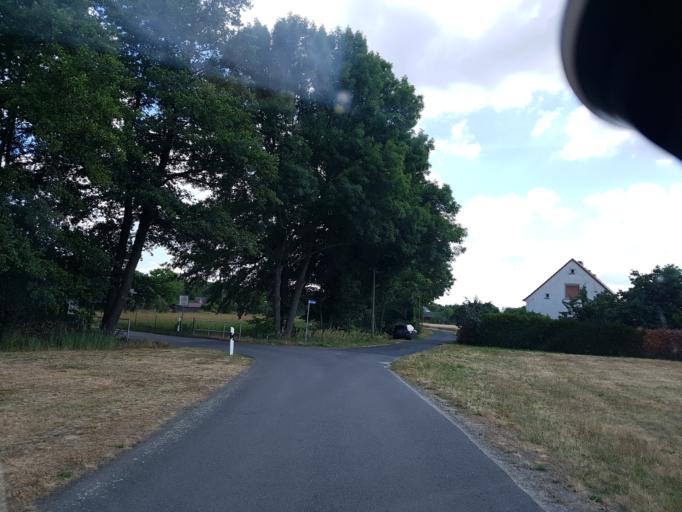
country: DE
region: Brandenburg
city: Altdobern
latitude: 51.6788
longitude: 14.0787
